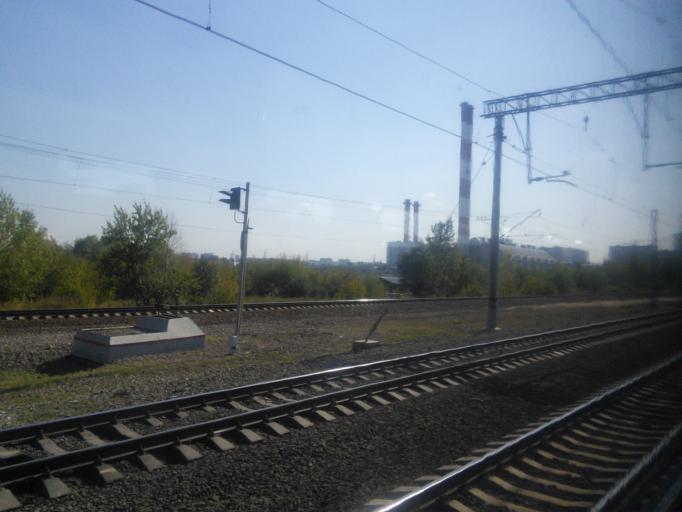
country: RU
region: Moskovskaya
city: Kur'yanovo
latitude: 55.6492
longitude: 37.7008
